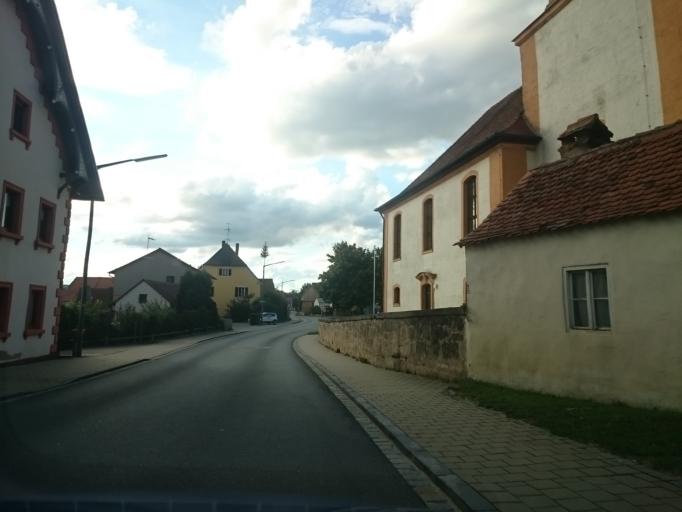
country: DE
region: Bavaria
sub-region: Regierungsbezirk Mittelfranken
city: Thalmassing
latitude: 49.1070
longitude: 11.1874
